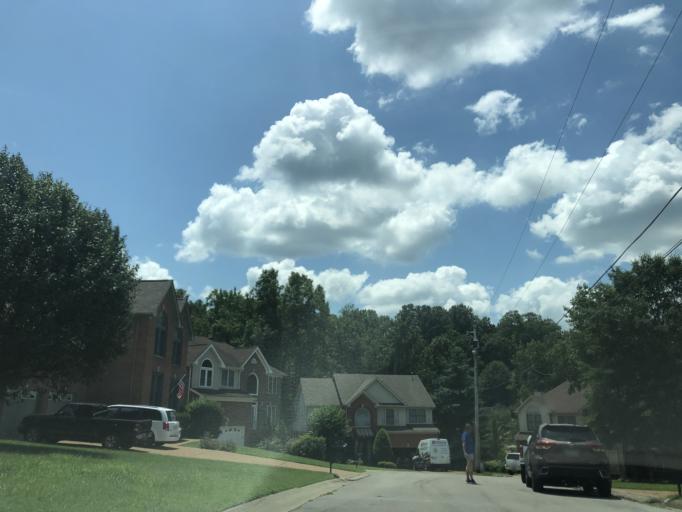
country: US
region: Tennessee
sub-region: Wilson County
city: Green Hill
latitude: 36.1922
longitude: -86.5906
